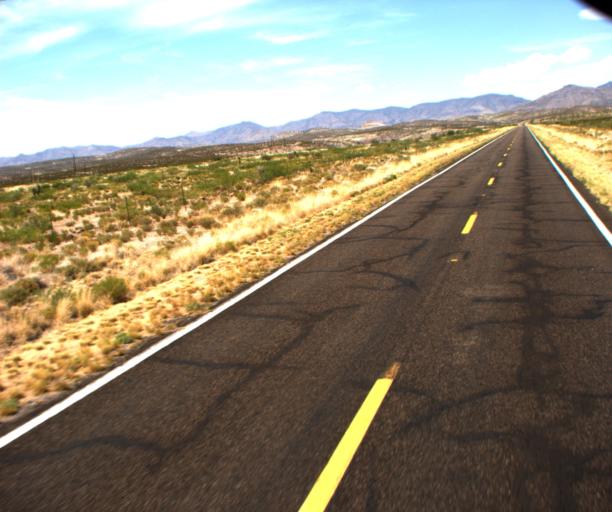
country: US
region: Arizona
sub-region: Greenlee County
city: Clifton
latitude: 32.9735
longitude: -109.1984
